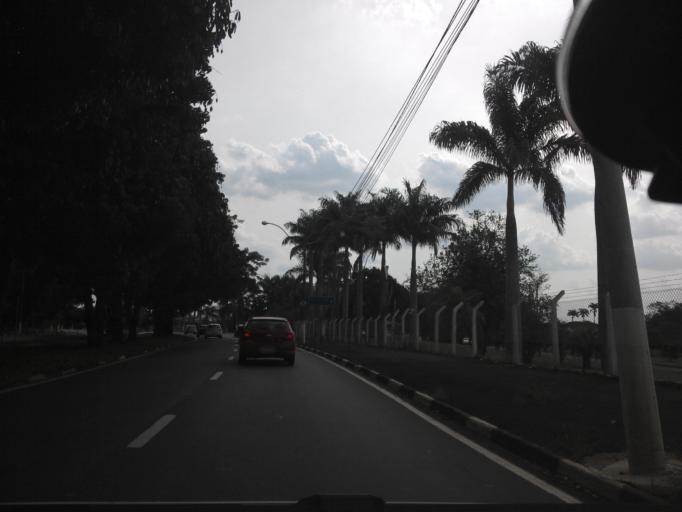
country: BR
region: Sao Paulo
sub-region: Campinas
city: Campinas
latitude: -22.8748
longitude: -47.0742
